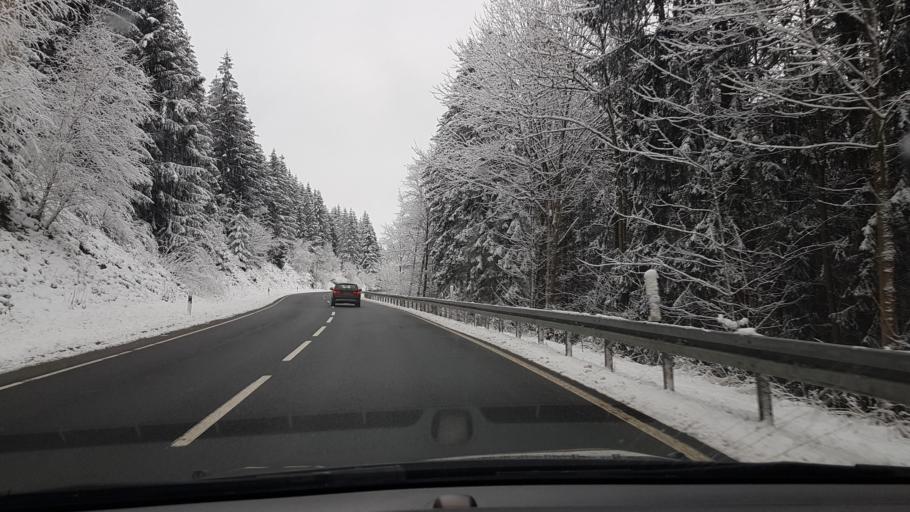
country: DE
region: Lower Saxony
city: Wildemann
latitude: 51.8088
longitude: 10.2646
